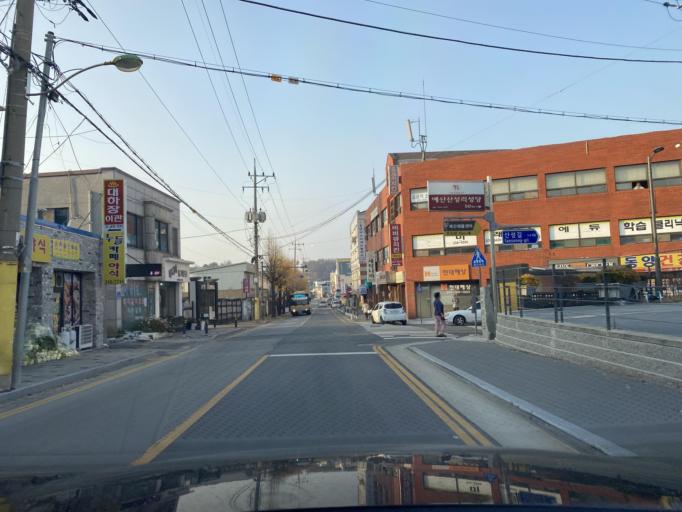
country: KR
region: Chungcheongnam-do
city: Yesan
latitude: 36.6870
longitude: 126.8318
